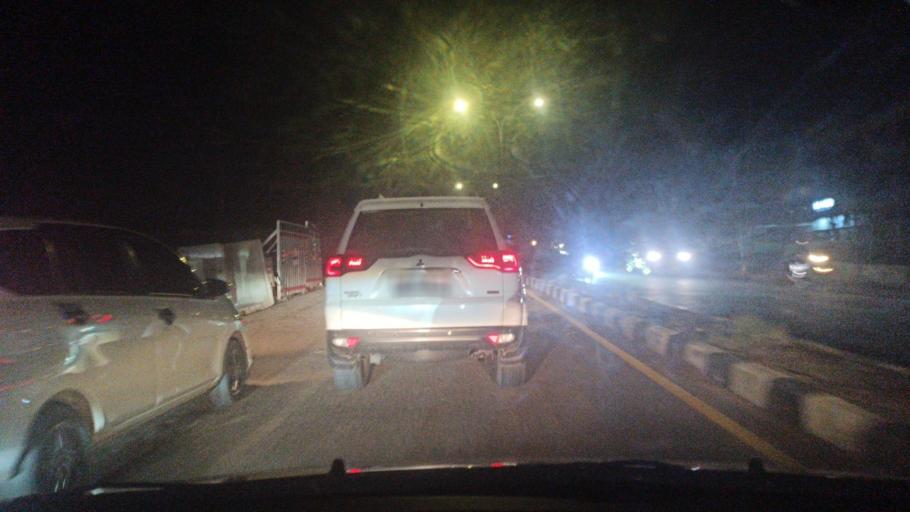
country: ID
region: South Sumatra
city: Palembang
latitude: -2.9528
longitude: 104.7546
